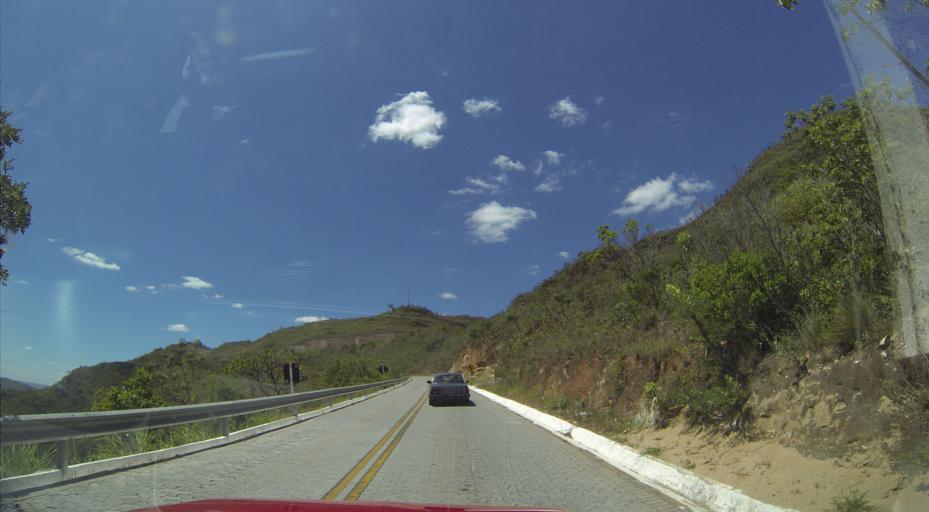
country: BR
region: Minas Gerais
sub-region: Conceicao Do Mato Dentro
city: Conceicao do Mato Dentro
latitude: -19.3084
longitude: -43.6071
